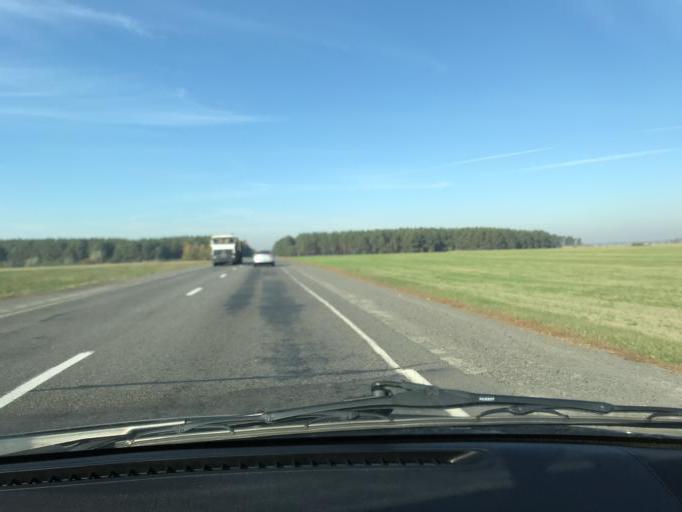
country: BY
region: Brest
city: Luninyets
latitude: 52.2554
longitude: 27.0488
